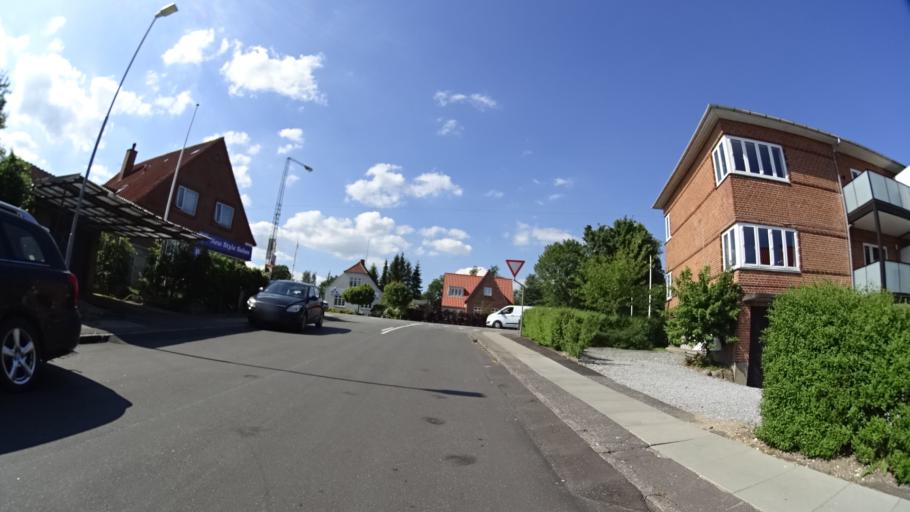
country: DK
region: Central Jutland
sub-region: Arhus Kommune
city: Stavtrup
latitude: 56.1542
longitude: 10.1569
